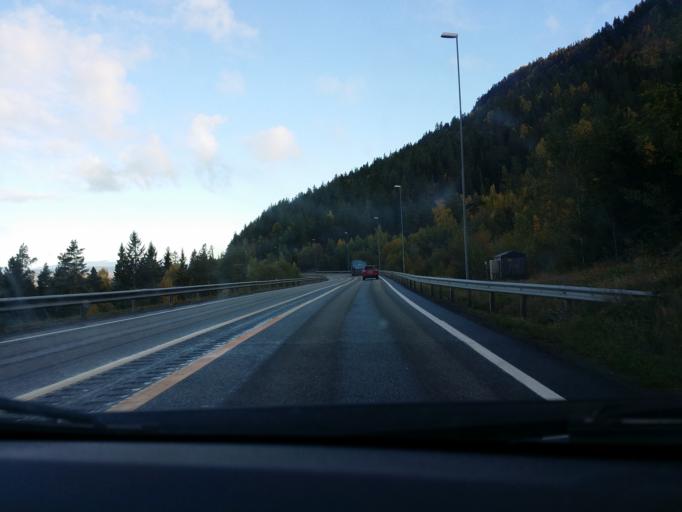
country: NO
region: Buskerud
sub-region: Hole
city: Vik
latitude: 60.0101
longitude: 10.2709
